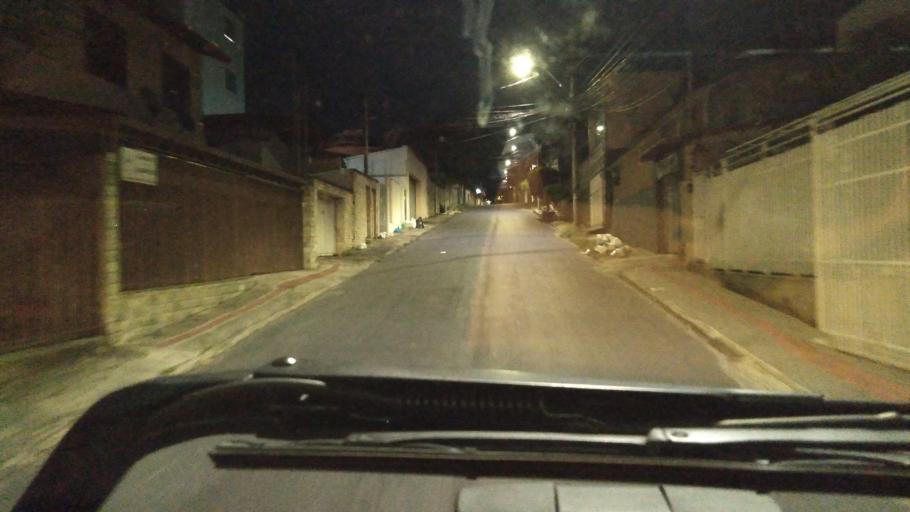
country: BR
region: Minas Gerais
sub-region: Belo Horizonte
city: Belo Horizonte
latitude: -19.9169
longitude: -43.9790
